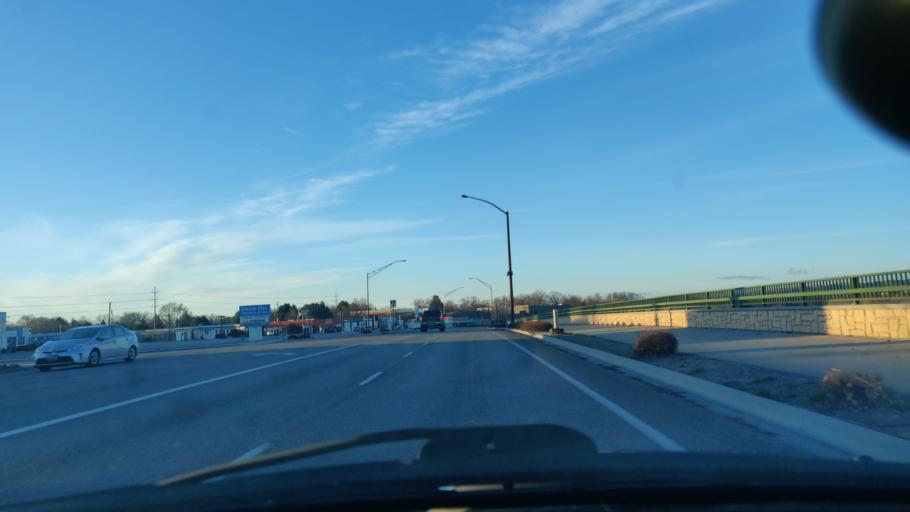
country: US
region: Idaho
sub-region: Ada County
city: Boise
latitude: 43.5770
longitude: -116.1955
